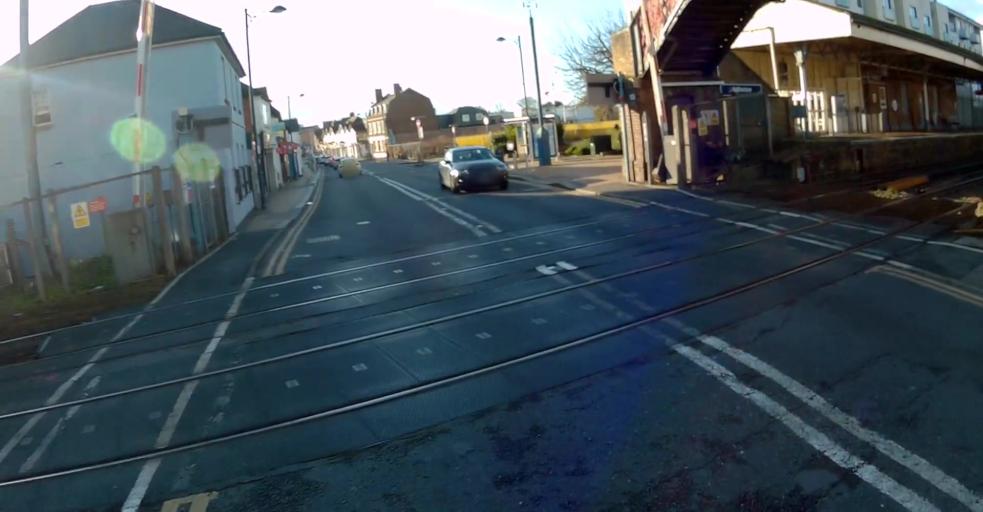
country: GB
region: England
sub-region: Surrey
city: Addlestone
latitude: 51.3729
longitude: -0.4841
